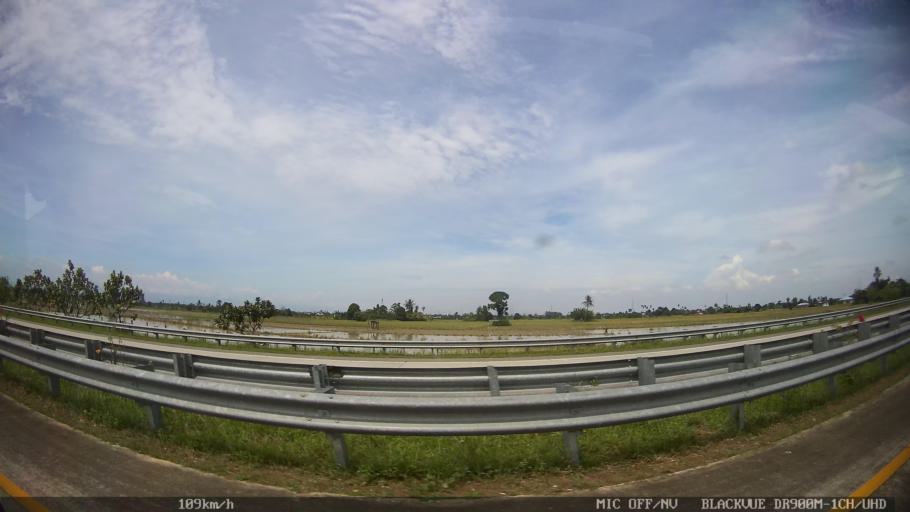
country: ID
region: North Sumatra
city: Percut
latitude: 3.5704
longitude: 98.8479
